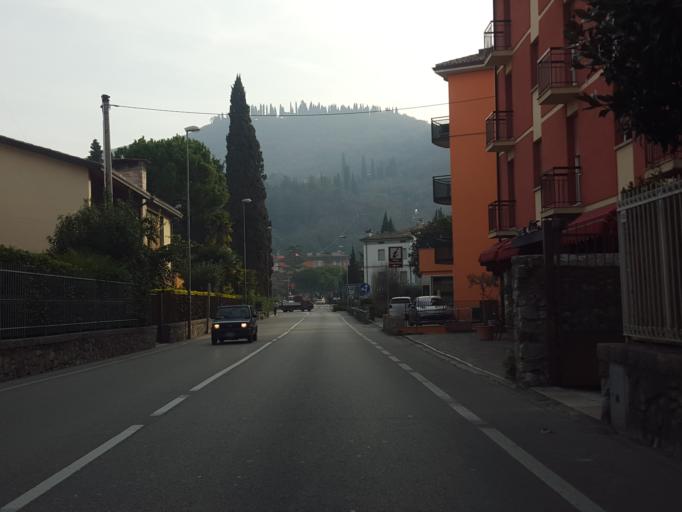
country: IT
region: Veneto
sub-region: Provincia di Verona
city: Garda
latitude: 45.5763
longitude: 10.7073
